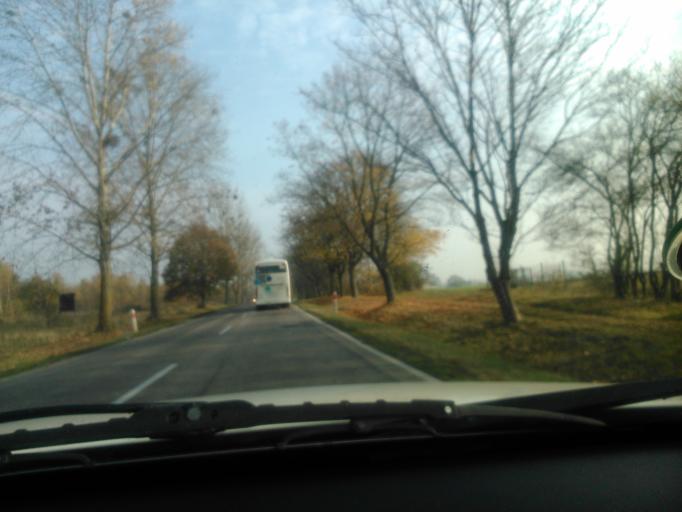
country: PL
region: Kujawsko-Pomorskie
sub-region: Powiat brodnicki
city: Brodnica
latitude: 53.2580
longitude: 19.3353
